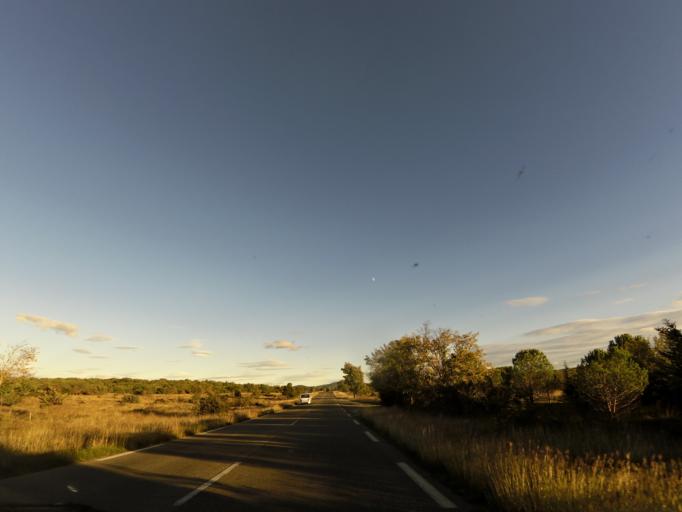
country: FR
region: Languedoc-Roussillon
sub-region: Departement du Gard
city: Saint-Hippolyte-du-Fort
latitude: 43.9522
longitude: 3.8790
